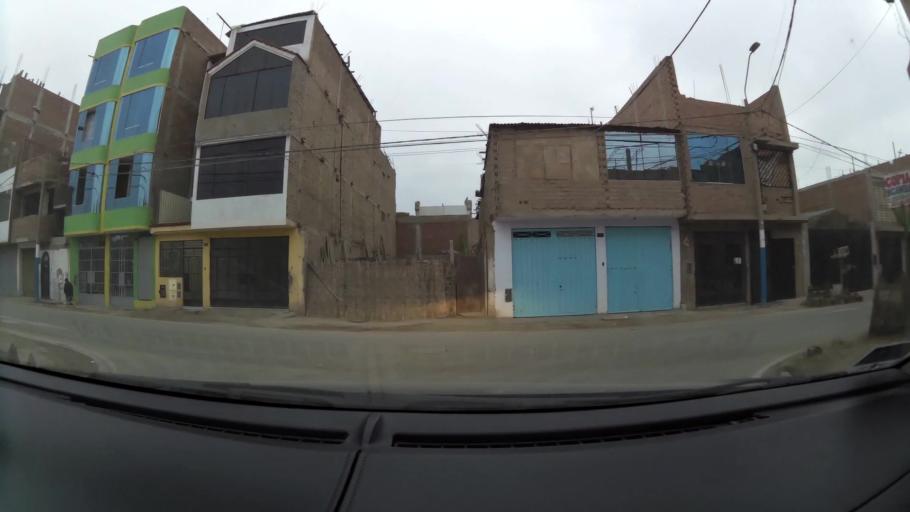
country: PE
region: Lima
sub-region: Lima
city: Independencia
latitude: -11.9781
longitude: -77.0976
